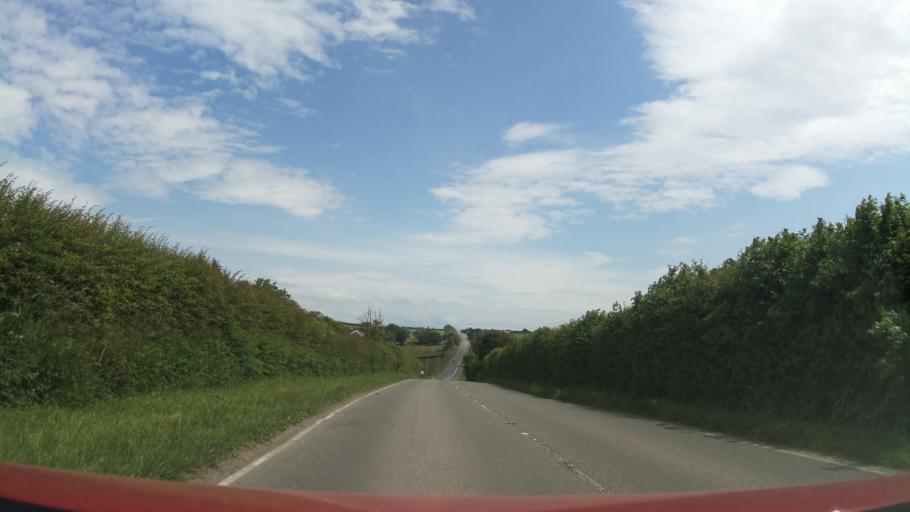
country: GB
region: Wales
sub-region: Vale of Glamorgan
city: Llangan
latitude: 51.4823
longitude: -3.5369
